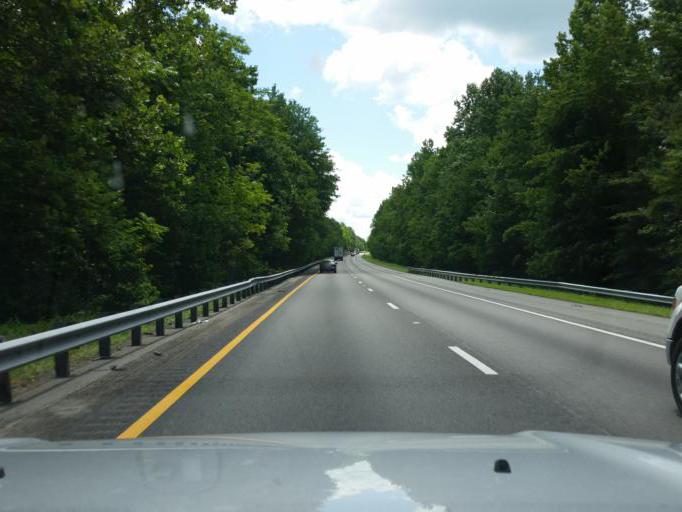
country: US
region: Virginia
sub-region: King William County
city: West Point
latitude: 37.4016
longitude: -76.7816
